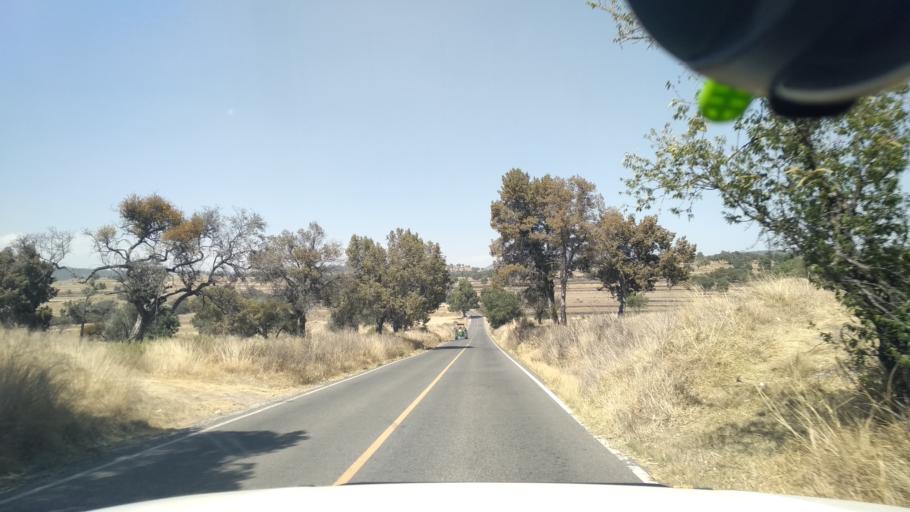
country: MX
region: Puebla
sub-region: San Matias Tlalancaleca
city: San Francisco Tlaloc
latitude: 19.3992
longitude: -98.4824
